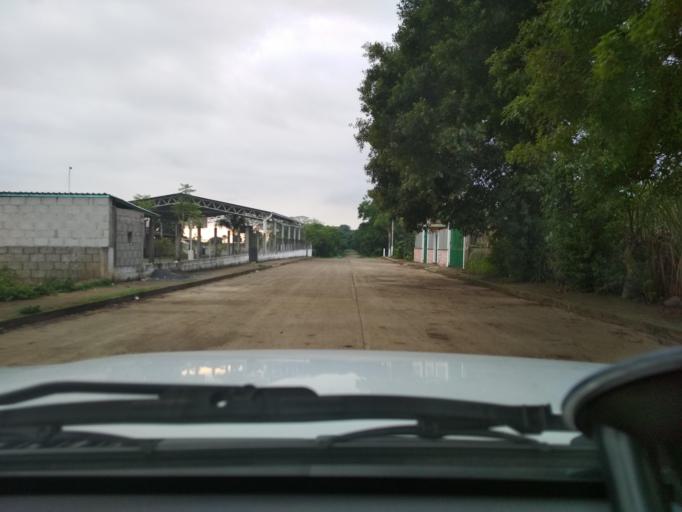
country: MX
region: Veracruz
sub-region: Fortin
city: Monte Salas
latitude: 18.9228
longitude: -97.0438
